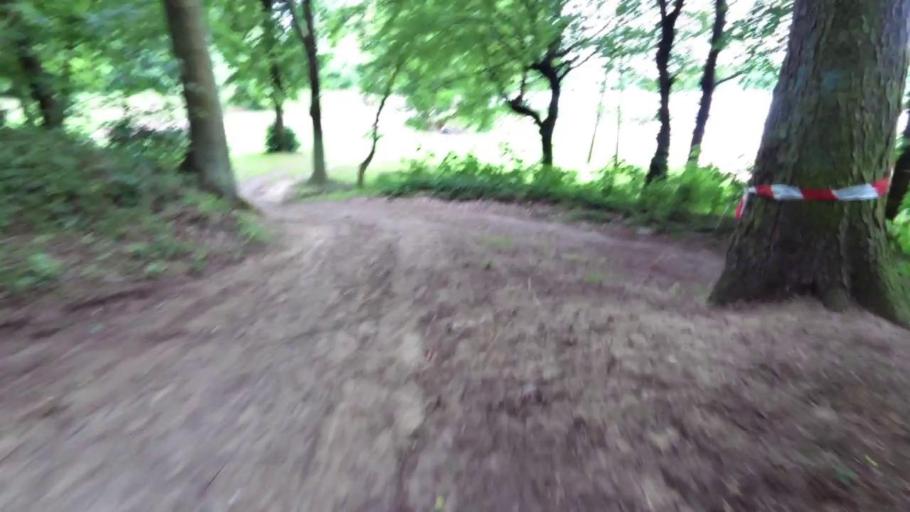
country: PL
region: West Pomeranian Voivodeship
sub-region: Powiat stargardzki
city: Chociwel
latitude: 53.4600
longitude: 15.3400
